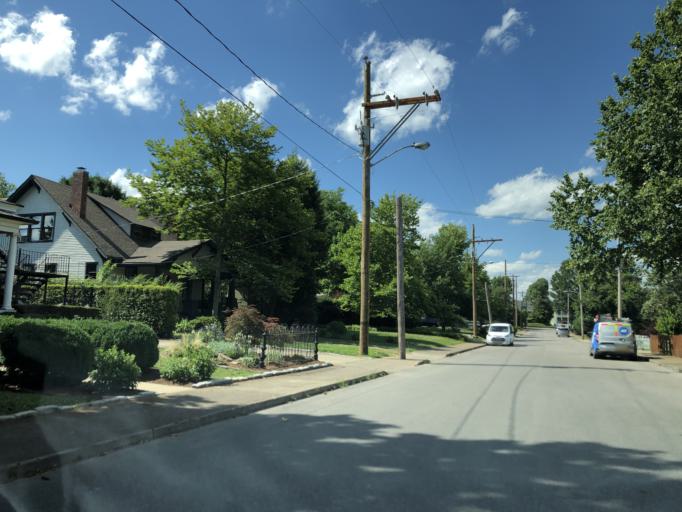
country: US
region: Tennessee
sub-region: Davidson County
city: Nashville
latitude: 36.1812
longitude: -86.7388
